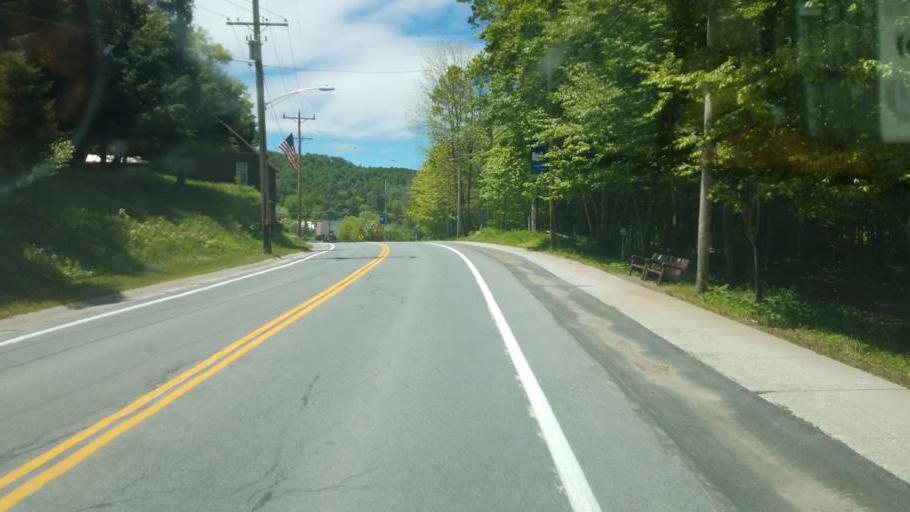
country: US
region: New York
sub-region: Hamilton County
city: Lake Pleasant
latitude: 43.7540
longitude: -74.7928
